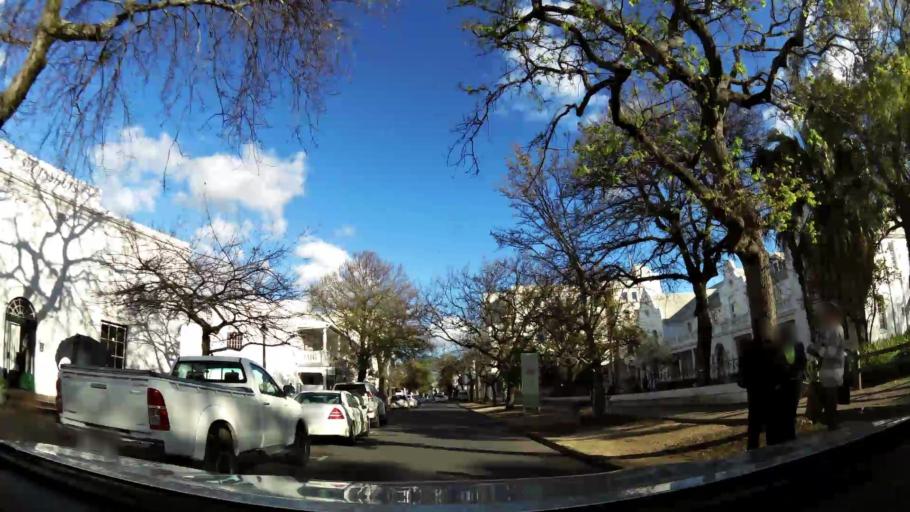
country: ZA
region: Western Cape
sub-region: Cape Winelands District Municipality
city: Stellenbosch
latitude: -33.9358
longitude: 18.8627
